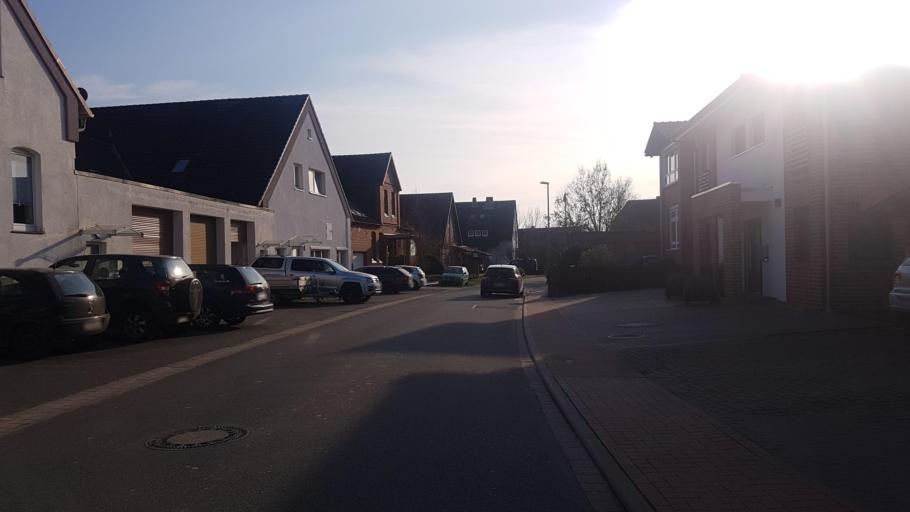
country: DE
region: Lower Saxony
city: Ronnenberg
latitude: 52.2963
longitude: 9.6688
